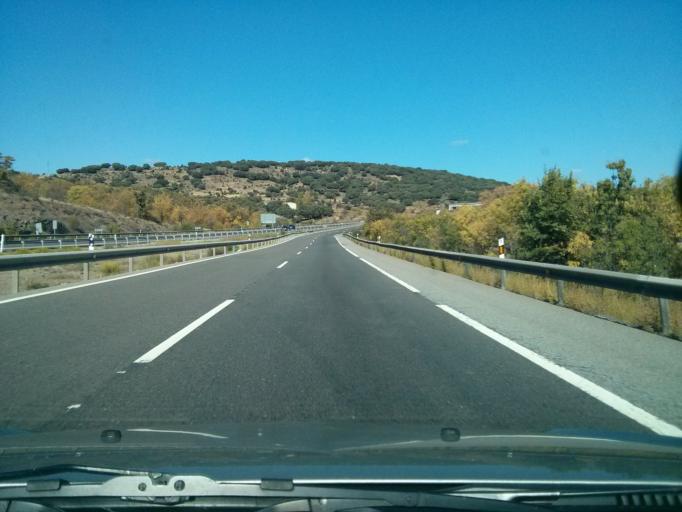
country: ES
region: Madrid
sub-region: Provincia de Madrid
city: Buitrago del Lozoya
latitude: 40.9458
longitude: -3.6372
